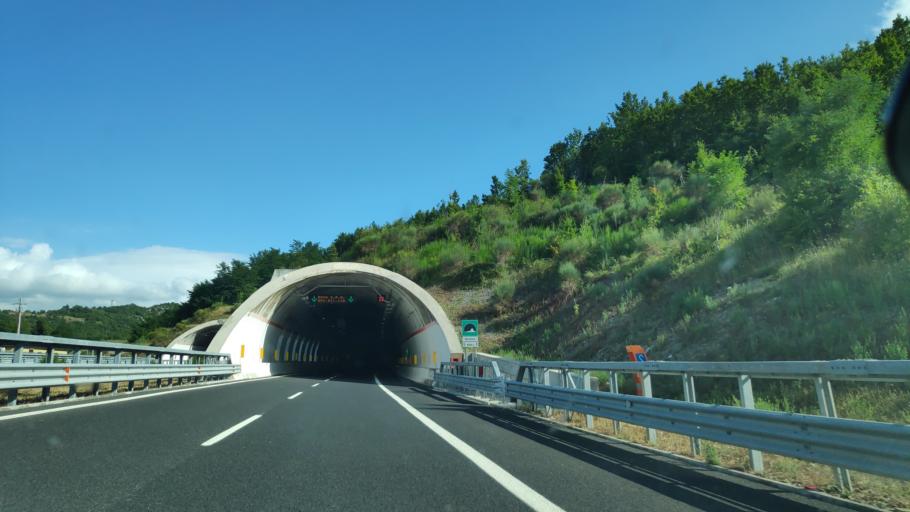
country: IT
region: Campania
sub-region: Provincia di Salerno
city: Casalbuono
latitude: 40.2283
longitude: 15.6694
